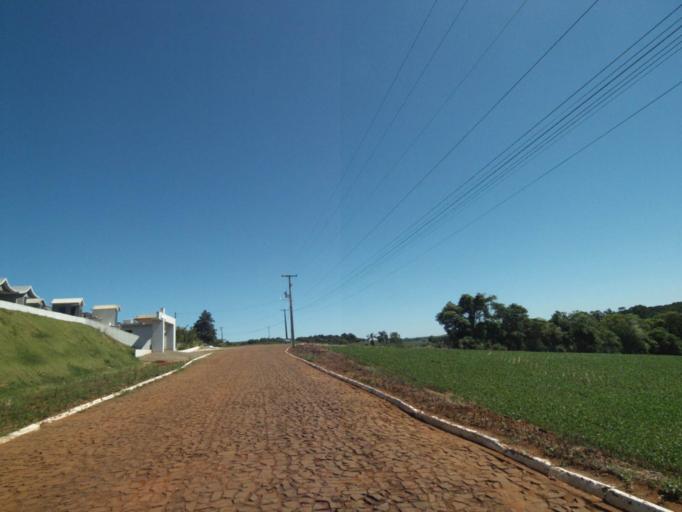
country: BR
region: Parana
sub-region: Pato Branco
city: Pato Branco
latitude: -26.2588
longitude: -52.7823
